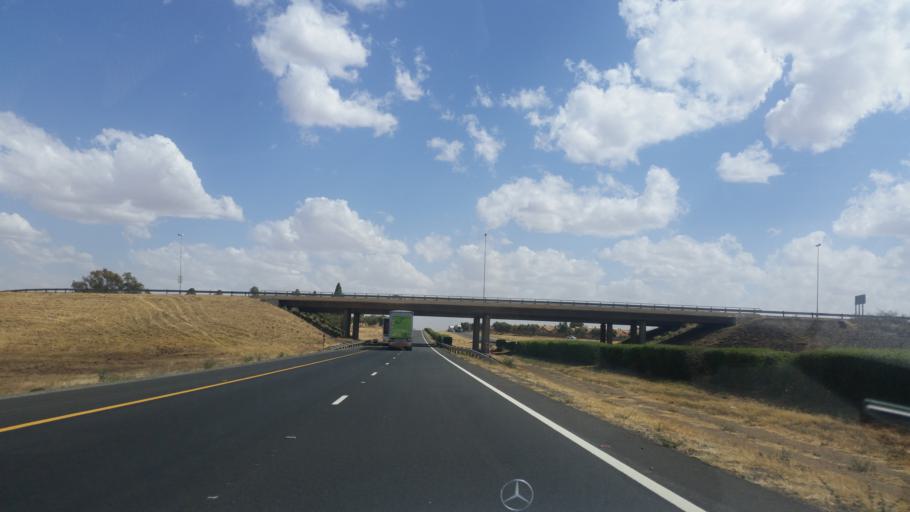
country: ZA
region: Orange Free State
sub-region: Mangaung Metropolitan Municipality
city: Bloemfontein
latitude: -29.0895
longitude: 26.1718
